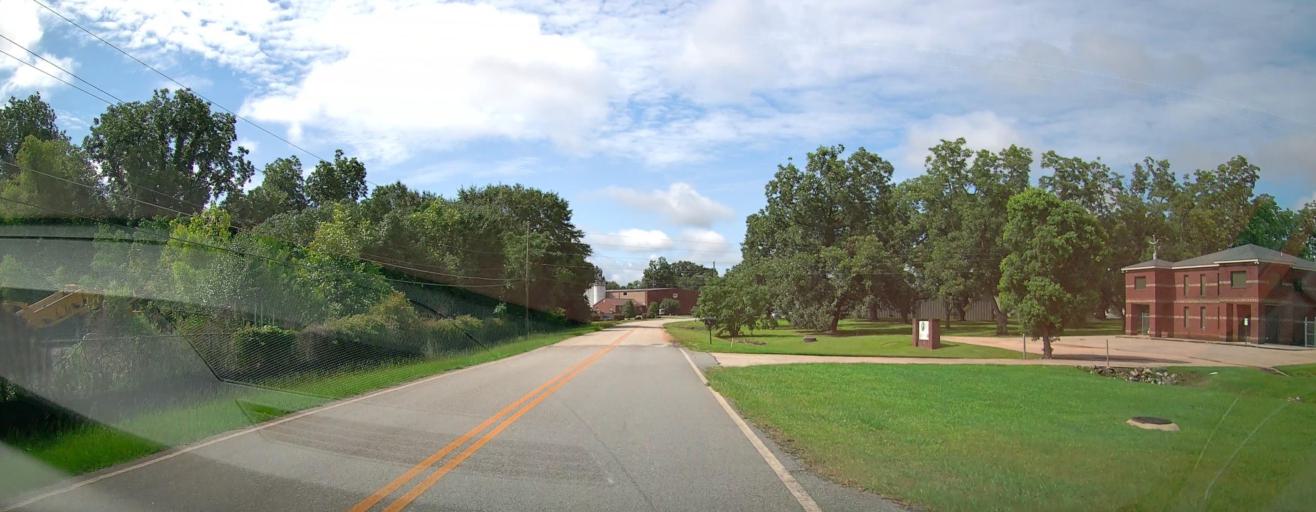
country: US
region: Georgia
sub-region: Peach County
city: Byron
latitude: 32.6498
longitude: -83.7364
